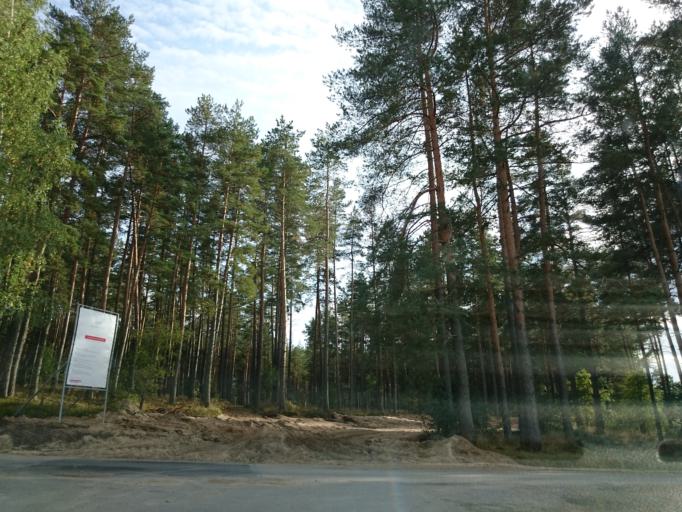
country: LV
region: Adazi
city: Adazi
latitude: 57.0514
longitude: 24.3490
